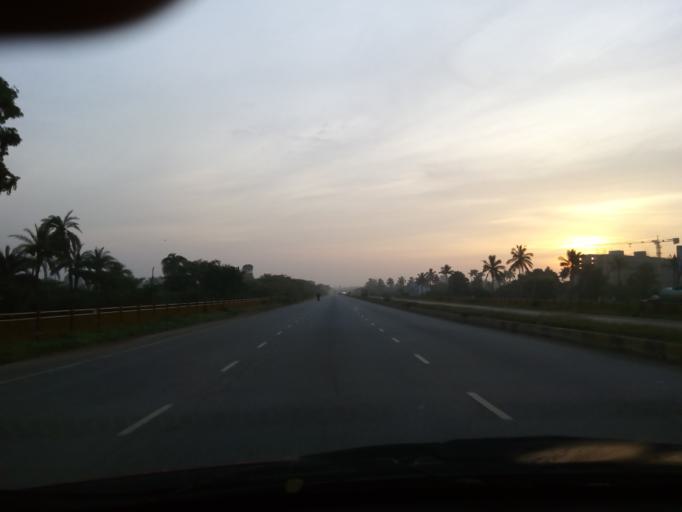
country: IN
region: Karnataka
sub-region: Bangalore Rural
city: Devanhalli
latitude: 13.2317
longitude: 77.6922
